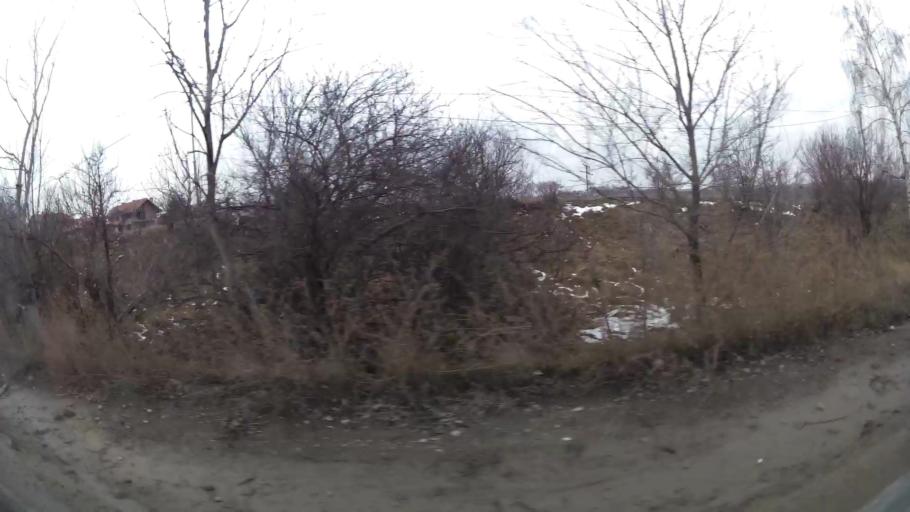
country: BG
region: Sofiya
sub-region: Obshtina Bozhurishte
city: Bozhurishte
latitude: 42.6993
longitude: 23.2303
